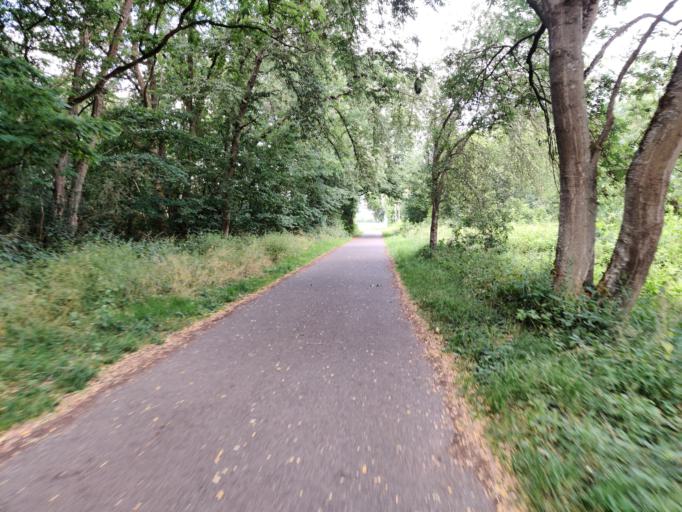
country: DE
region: Rheinland-Pfalz
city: Roxheim
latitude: 49.8712
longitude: 7.8098
